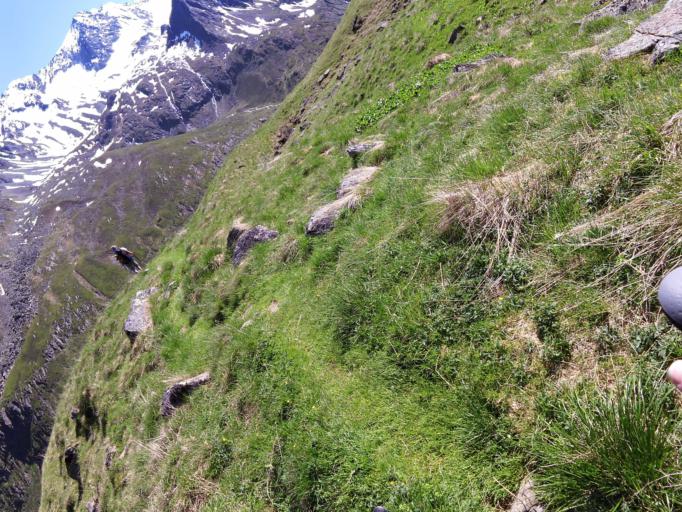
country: AT
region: Tyrol
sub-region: Politischer Bezirk Innsbruck Land
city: Gries im Sellrain
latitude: 47.0941
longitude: 11.1755
